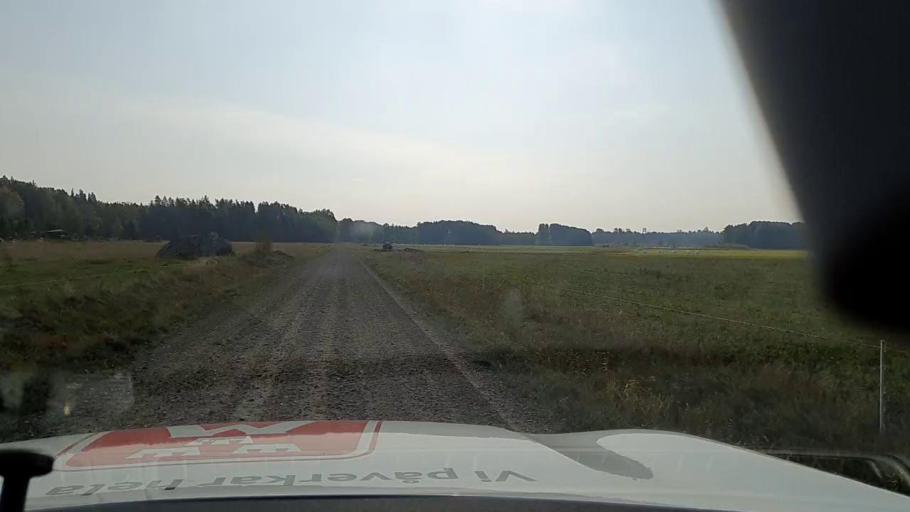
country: SE
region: Vaestmanland
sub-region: Kungsors Kommun
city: Kungsoer
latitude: 59.3541
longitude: 16.1596
